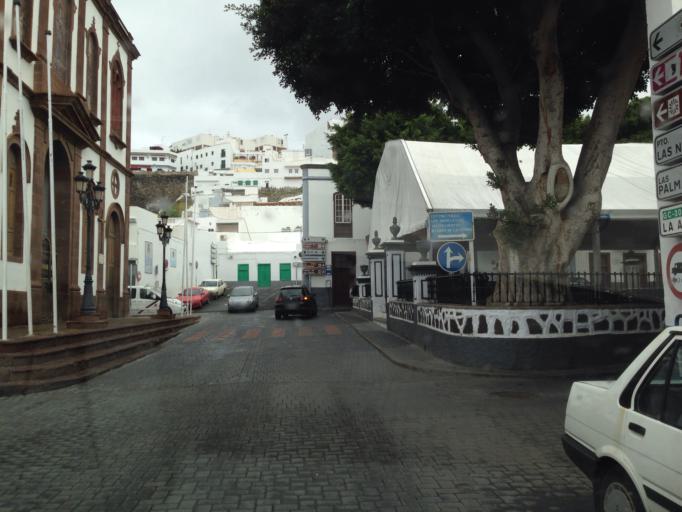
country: ES
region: Canary Islands
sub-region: Provincia de Las Palmas
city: Agaete
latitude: 28.0998
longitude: -15.7008
